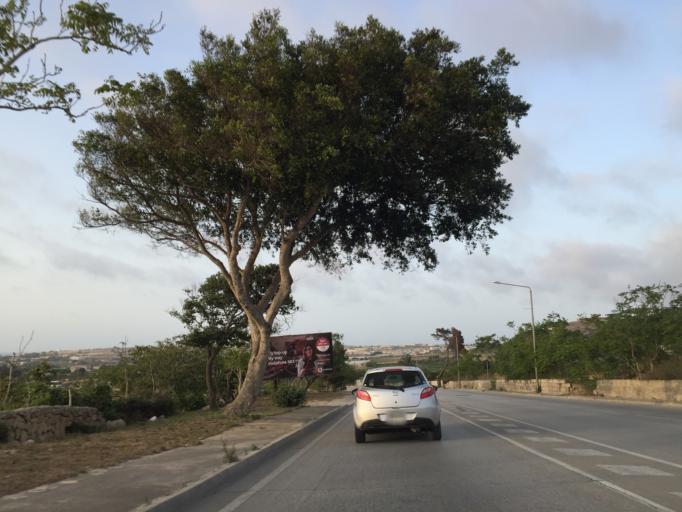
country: MT
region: Il-Mosta
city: Mosta
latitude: 35.9187
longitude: 14.4139
